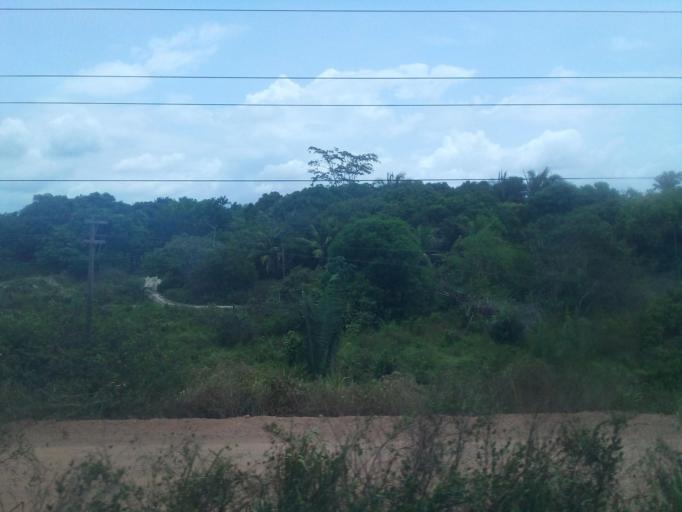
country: BR
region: Maranhao
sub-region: Santa Ines
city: Santa Ines
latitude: -3.7066
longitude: -45.5687
